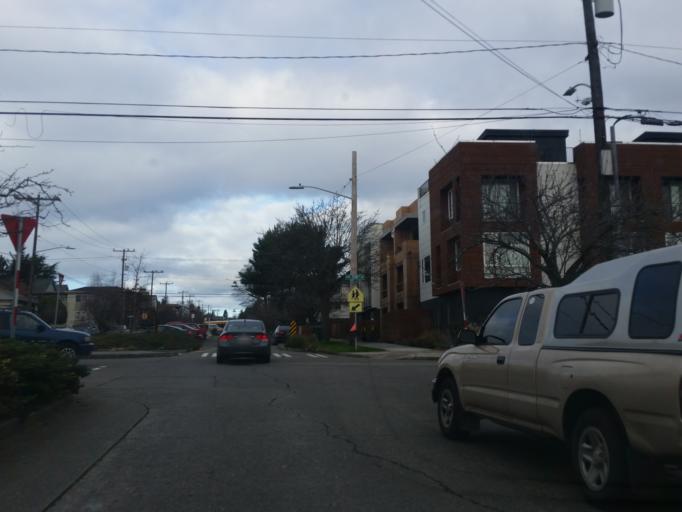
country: US
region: Washington
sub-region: King County
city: Seattle
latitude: 47.6706
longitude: -122.3735
